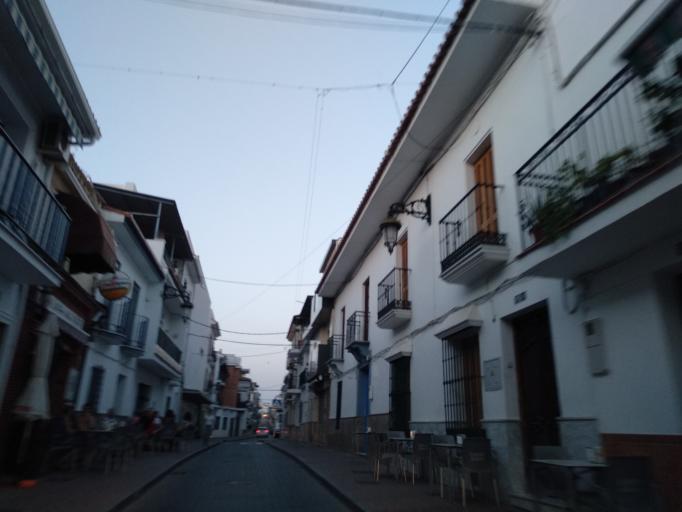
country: ES
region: Andalusia
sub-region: Provincia de Malaga
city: Cartama
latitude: 36.7100
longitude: -4.6333
